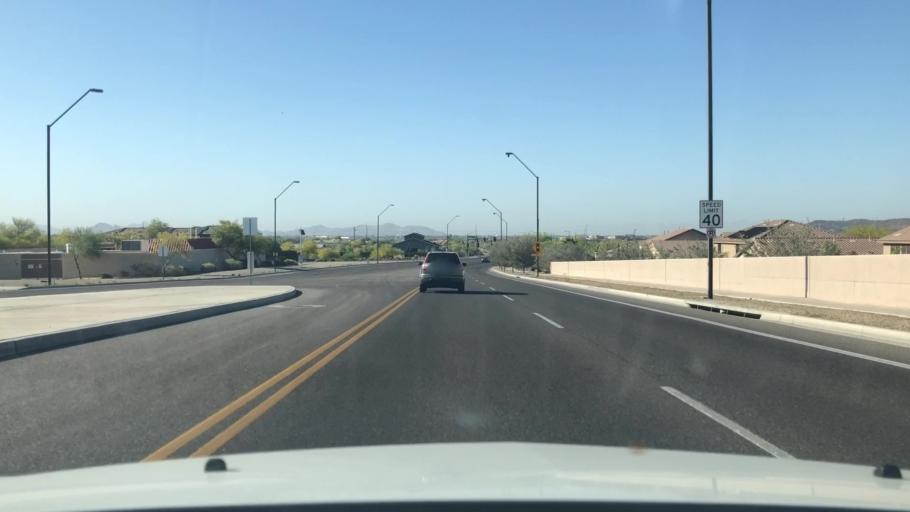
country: US
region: Arizona
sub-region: Maricopa County
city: Anthem
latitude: 33.7283
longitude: -112.0997
